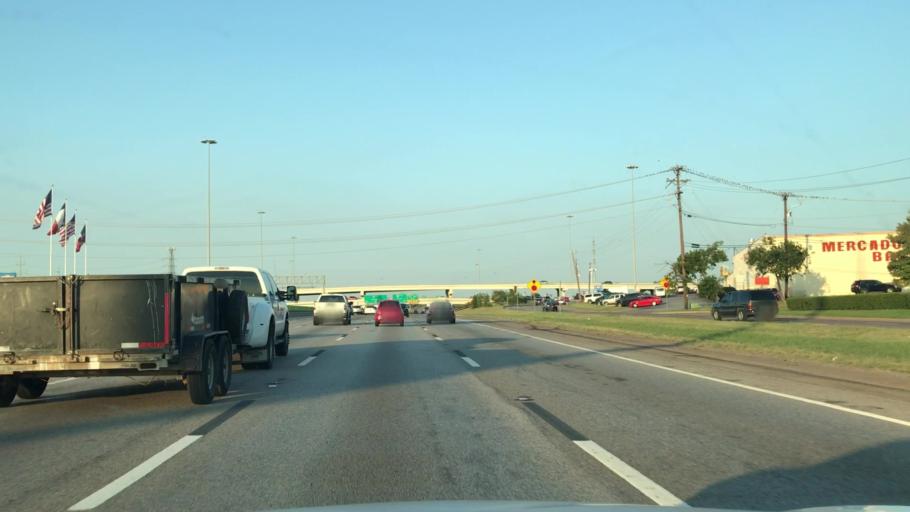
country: US
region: Texas
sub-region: Dallas County
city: Mesquite
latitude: 32.7968
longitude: -96.6870
